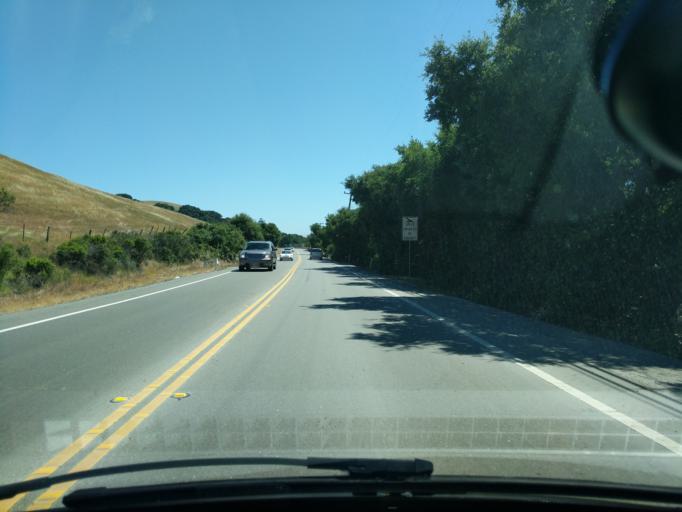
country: US
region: California
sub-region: Contra Costa County
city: San Ramon
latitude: 37.7563
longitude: -122.0293
